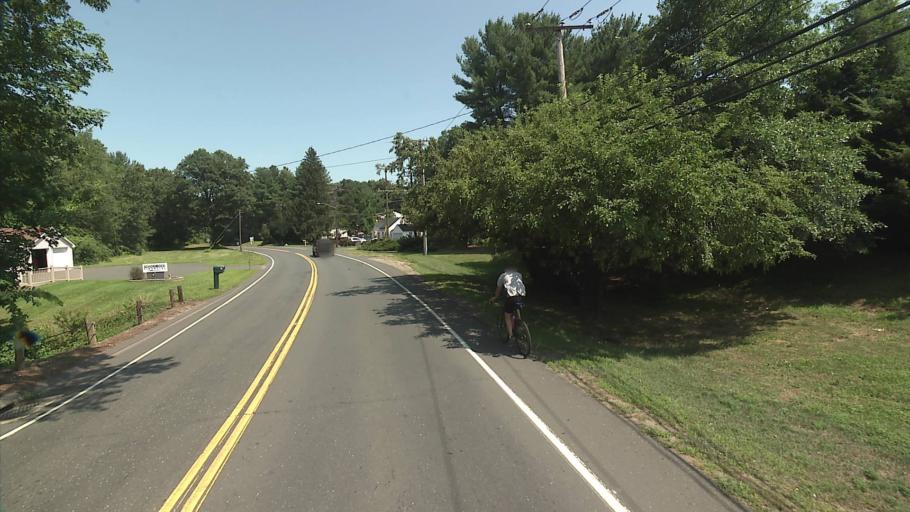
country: US
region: Connecticut
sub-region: Hartford County
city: Salmon Brook
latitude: 41.9535
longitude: -72.7838
